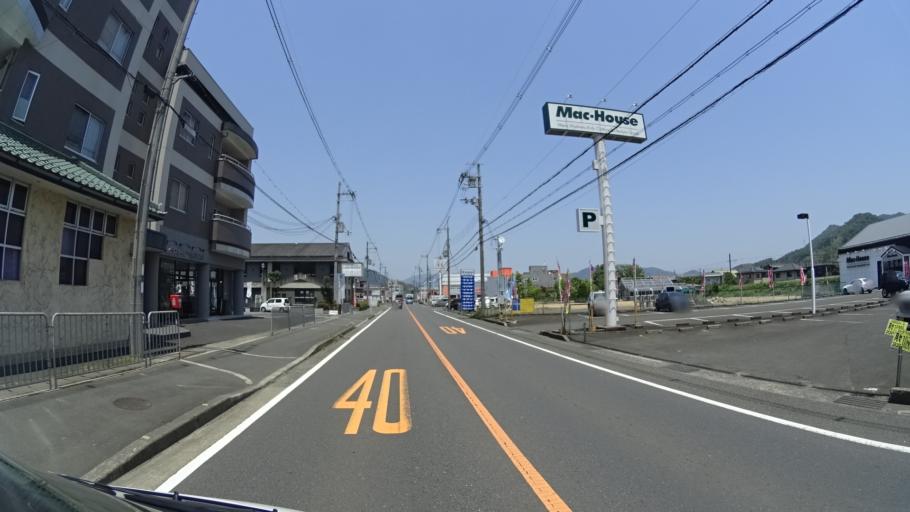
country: JP
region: Kyoto
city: Maizuru
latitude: 35.4231
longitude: 135.3294
